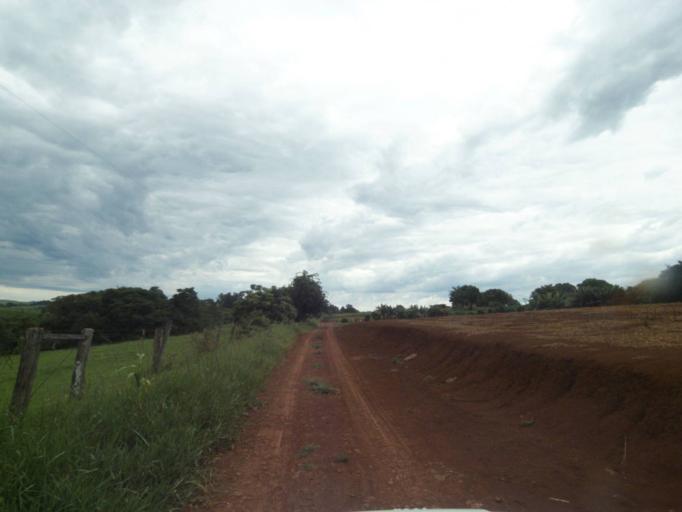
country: BR
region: Parana
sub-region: Guaraniacu
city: Guaraniacu
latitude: -24.9157
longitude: -52.9357
